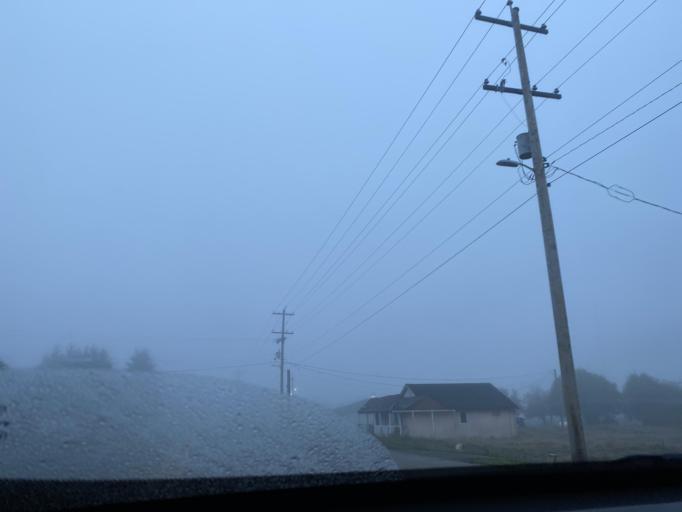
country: US
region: Washington
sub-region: Clallam County
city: Forks
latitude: 47.9438
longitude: -124.3855
